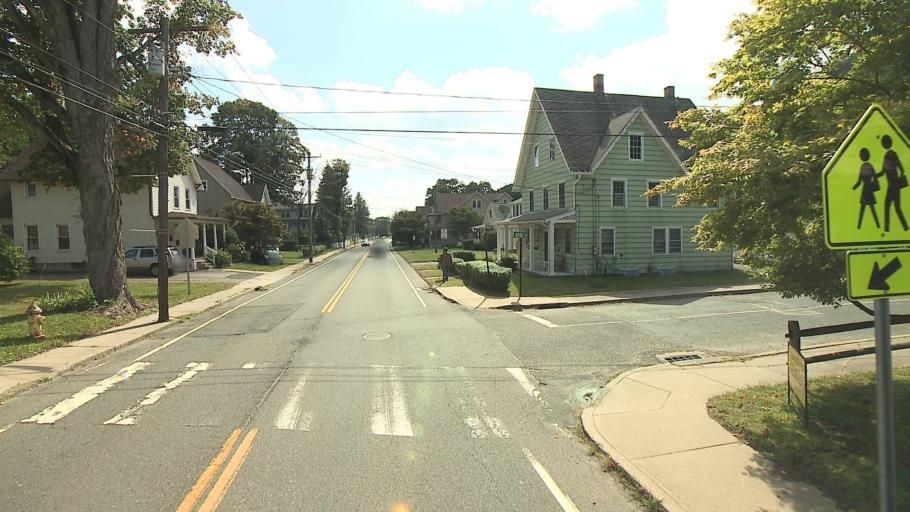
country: US
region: Connecticut
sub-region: New Haven County
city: Seymour
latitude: 41.3886
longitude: -73.0761
